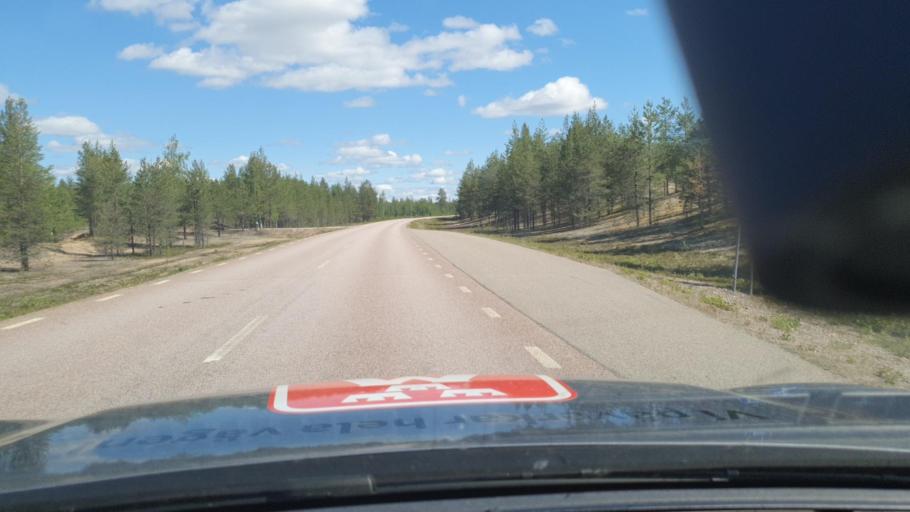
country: SE
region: Norrbotten
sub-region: Pajala Kommun
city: Pajala
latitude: 67.1805
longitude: 22.7024
